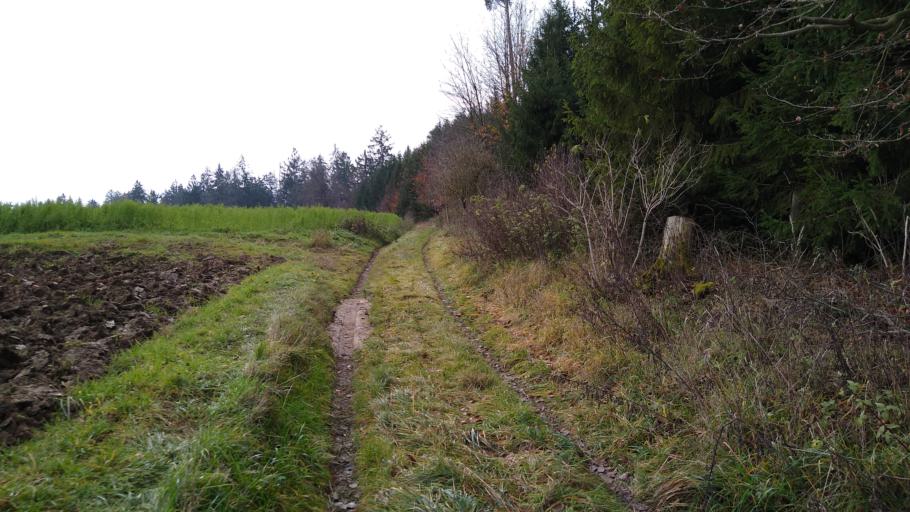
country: DE
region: Bavaria
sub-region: Upper Palatinate
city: Seubersdorf
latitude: 49.1491
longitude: 11.6352
